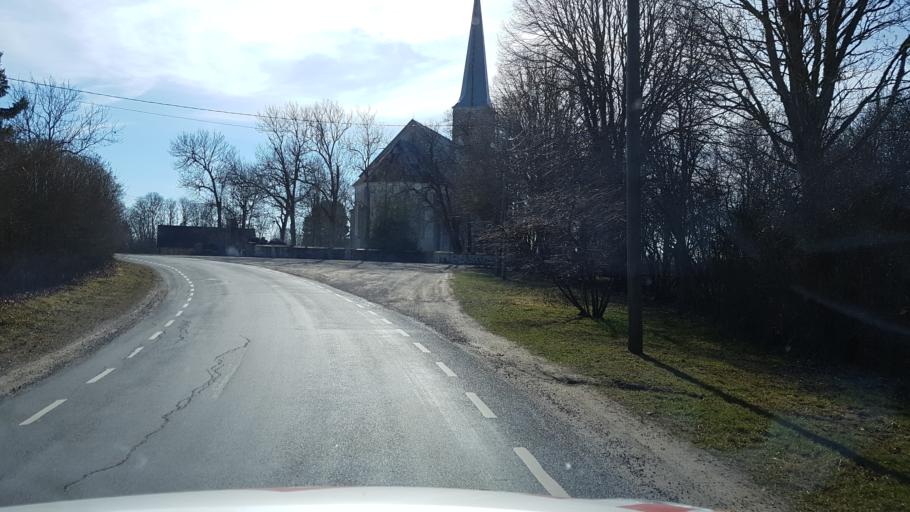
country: EE
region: Harju
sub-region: Nissi vald
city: Riisipere
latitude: 59.1045
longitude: 24.3112
